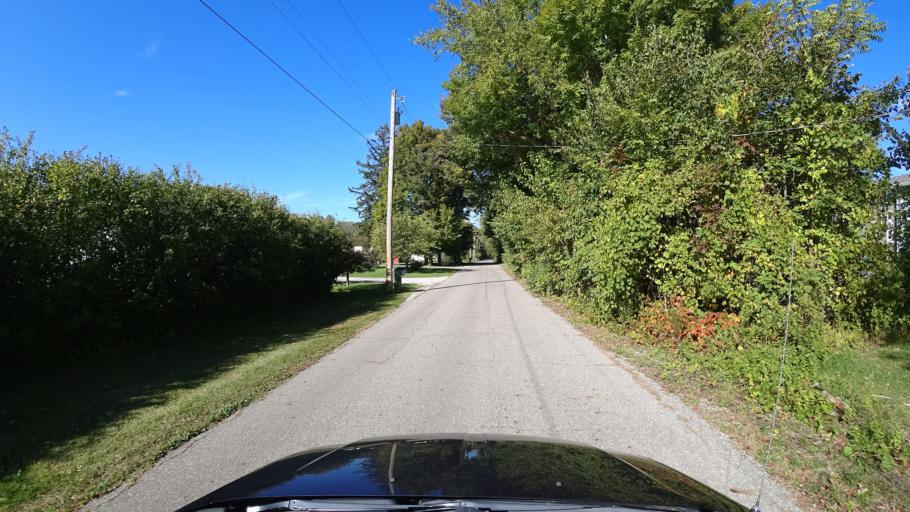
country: US
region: Indiana
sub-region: LaPorte County
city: Trail Creek
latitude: 41.7007
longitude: -86.8357
